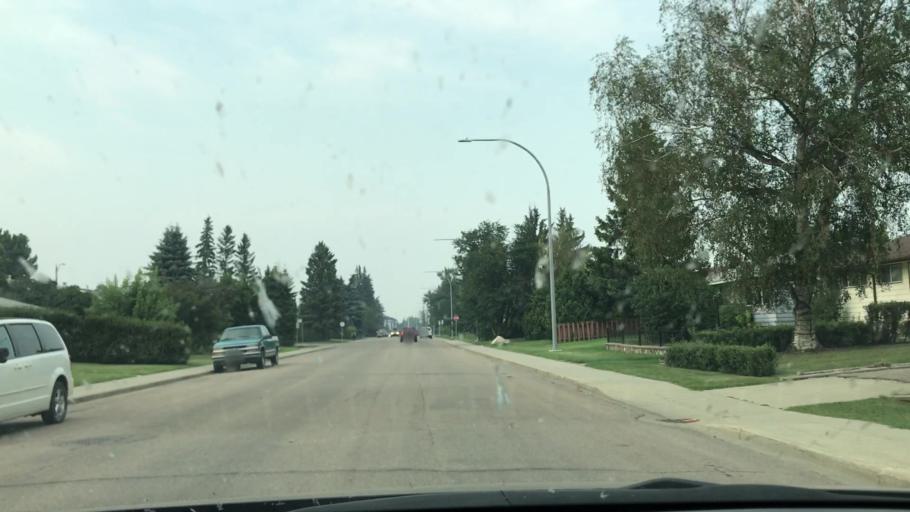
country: CA
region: Alberta
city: St. Albert
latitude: 53.5953
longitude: -113.5534
